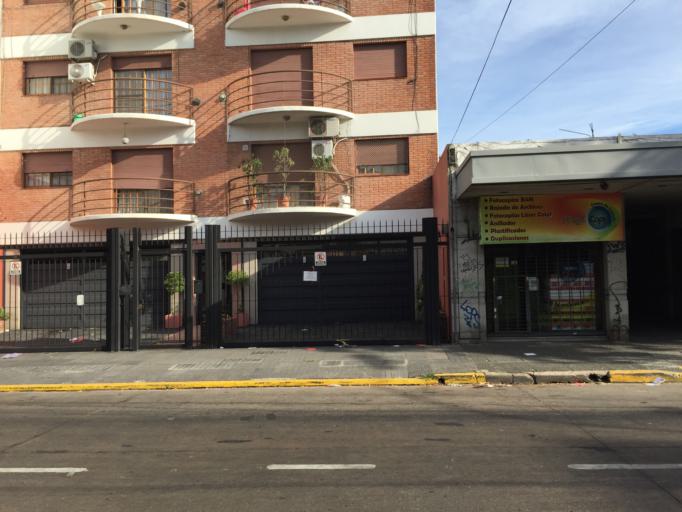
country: AR
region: Buenos Aires
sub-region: Partido de Vicente Lopez
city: Olivos
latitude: -34.5307
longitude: -58.4973
